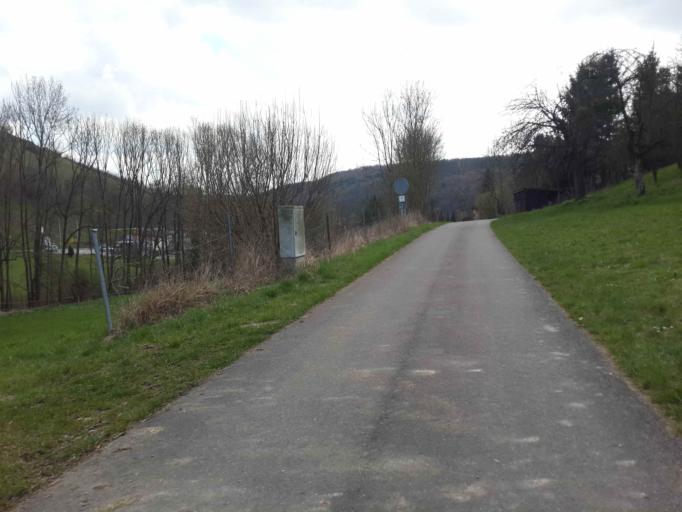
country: DE
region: Baden-Wuerttemberg
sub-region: Regierungsbezirk Stuttgart
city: Dorzbach
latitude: 49.3894
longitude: 9.7040
